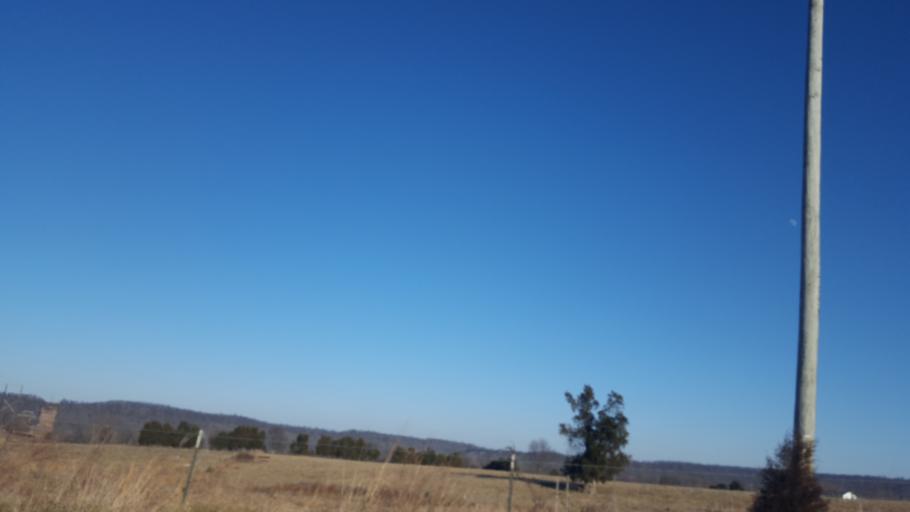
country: US
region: Kentucky
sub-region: Crittenden County
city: Marion
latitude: 37.4394
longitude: -88.0531
